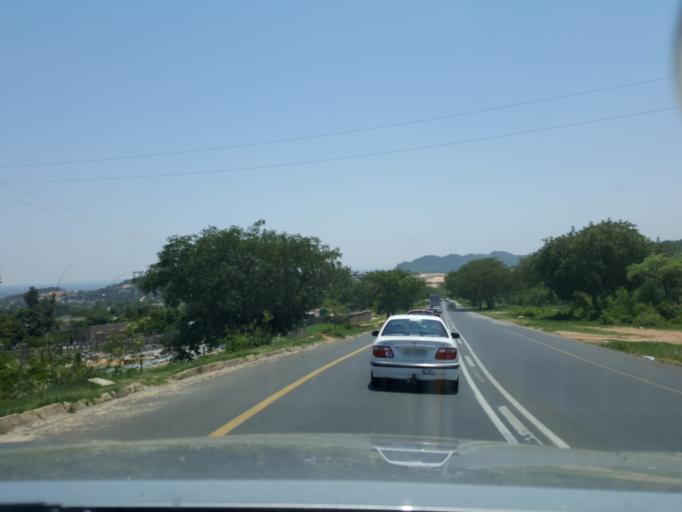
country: ZA
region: Limpopo
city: Thulamahashi
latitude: -24.8281
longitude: 31.0823
